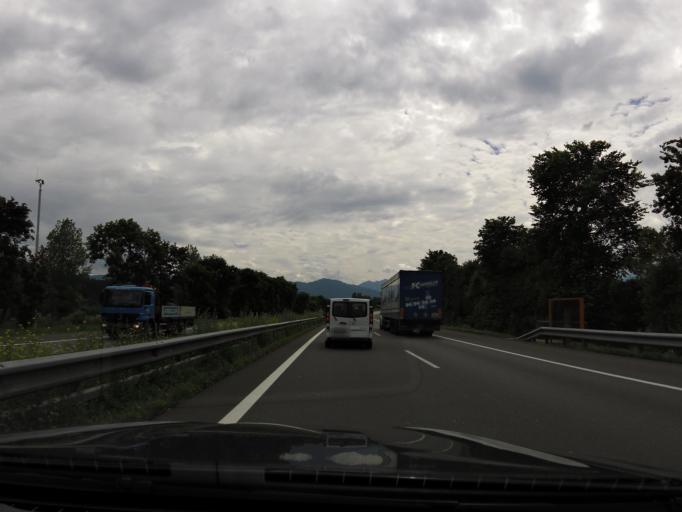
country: AT
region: Tyrol
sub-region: Politischer Bezirk Kufstein
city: Langkampfen
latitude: 47.5421
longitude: 12.1146
